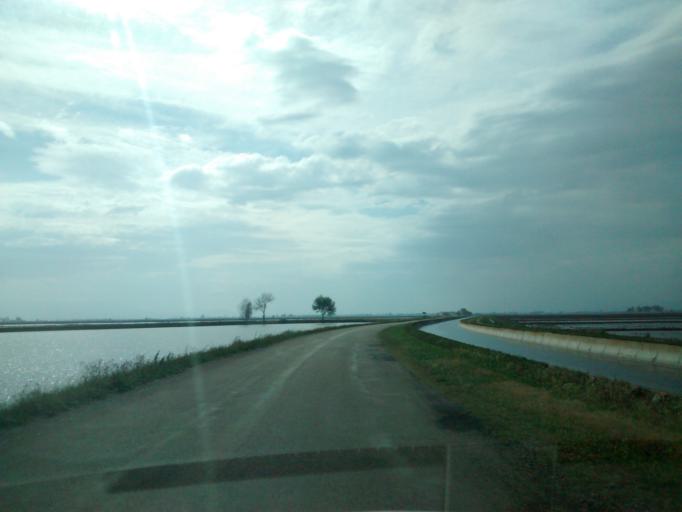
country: ES
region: Catalonia
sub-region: Provincia de Tarragona
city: Deltebre
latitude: 40.6901
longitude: 0.7827
